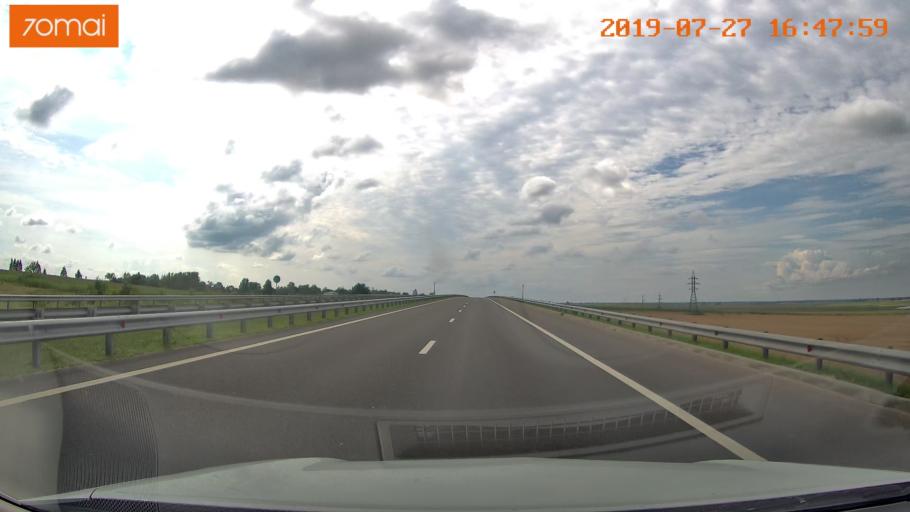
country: RU
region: Kaliningrad
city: Gvardeysk
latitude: 54.6691
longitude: 20.9801
